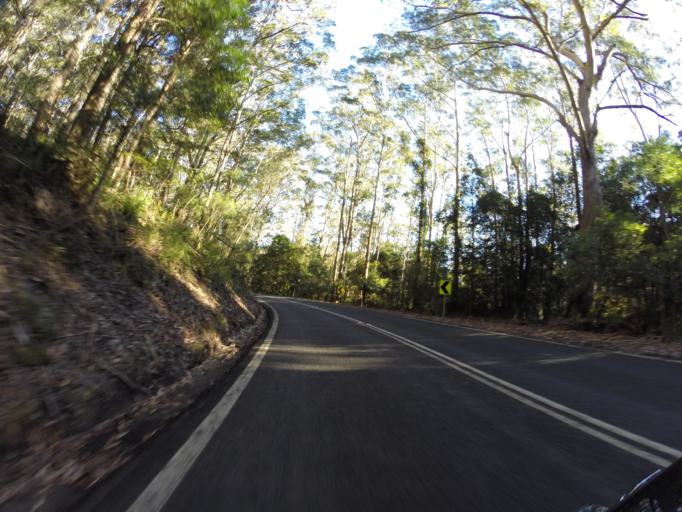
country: AU
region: New South Wales
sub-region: Wollongong
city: Helensburgh
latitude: -34.1837
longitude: 151.0095
